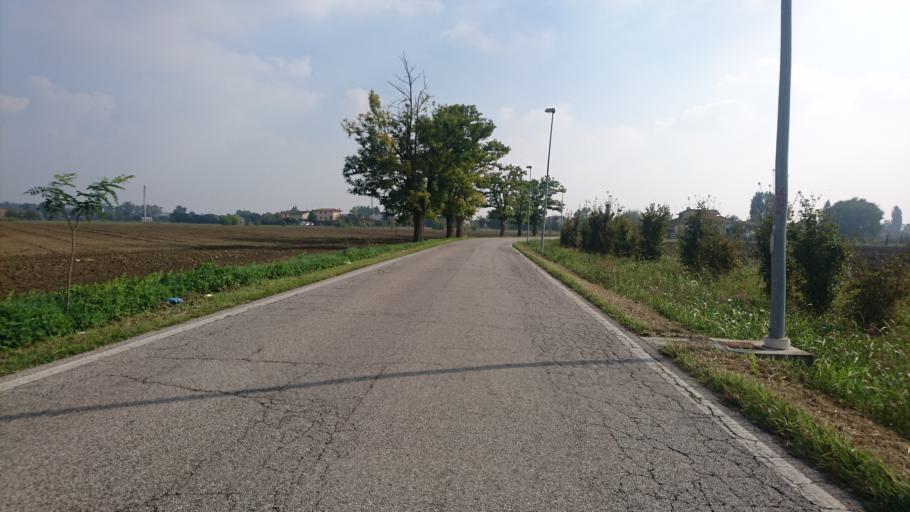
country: IT
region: Veneto
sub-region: Provincia di Rovigo
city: Rovigo
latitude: 45.0506
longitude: 11.7761
